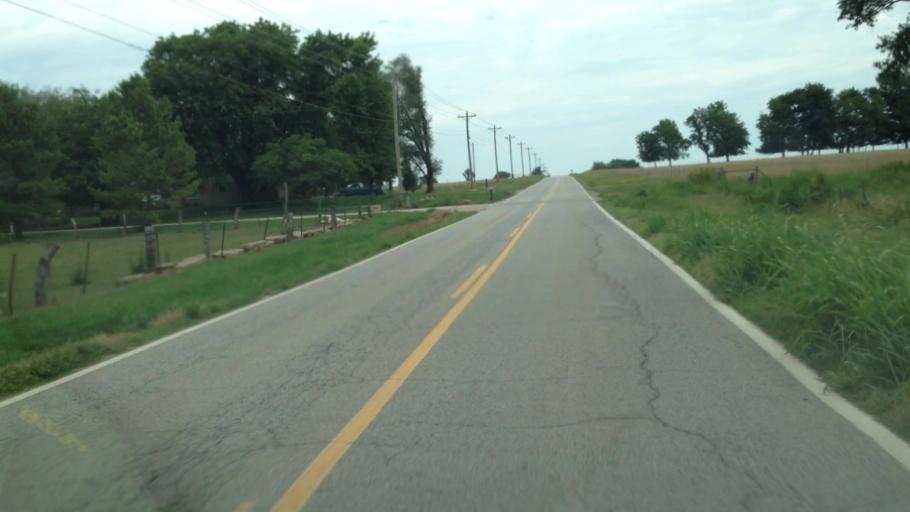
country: US
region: Oklahoma
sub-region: Delaware County
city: Cleora
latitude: 36.6048
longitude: -94.9634
